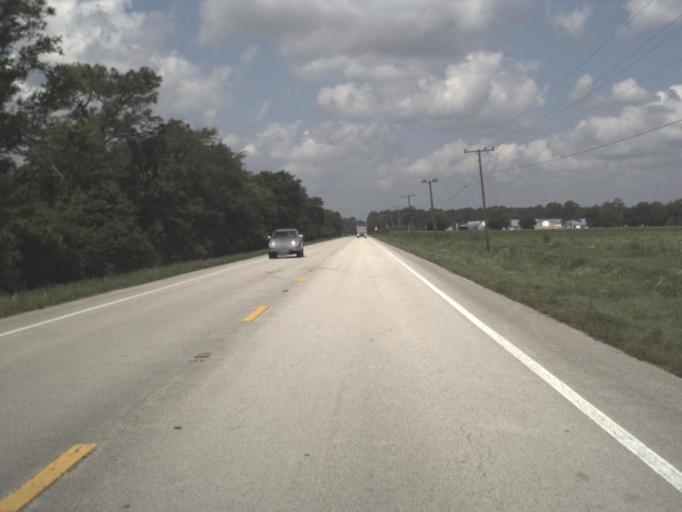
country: US
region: Florida
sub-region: Putnam County
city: East Palatka
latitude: 29.7257
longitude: -81.4559
